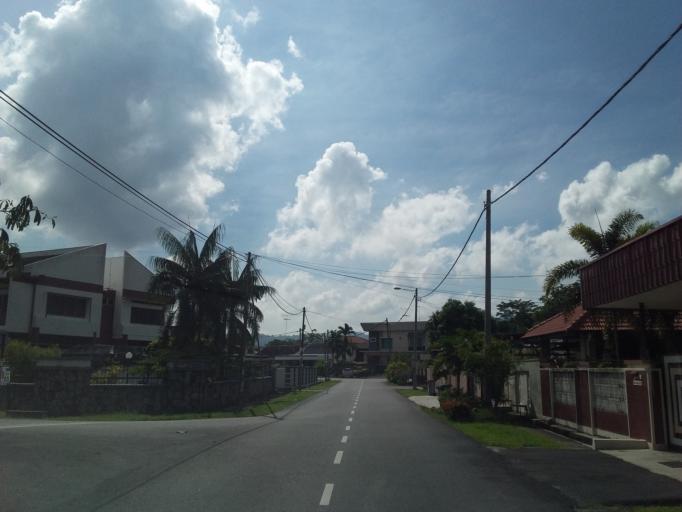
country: MY
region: Johor
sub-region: Daerah Batu Pahat
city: Batu Pahat
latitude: 1.8400
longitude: 102.9288
